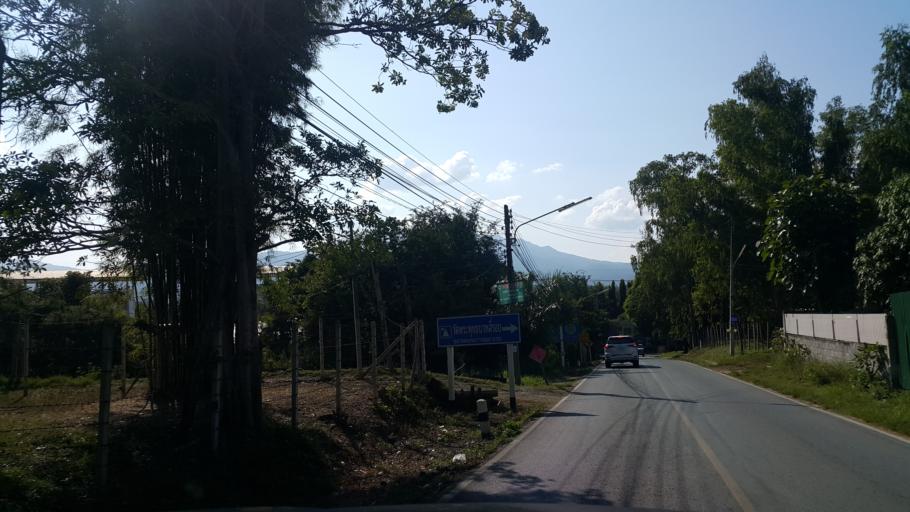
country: TH
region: Chiang Mai
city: San Sai
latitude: 18.9370
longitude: 98.9339
